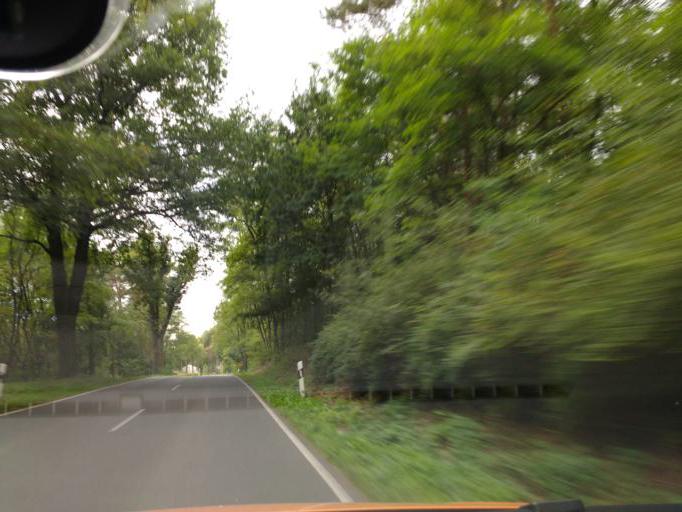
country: DE
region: Brandenburg
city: Reichenwalde
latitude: 52.2673
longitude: 14.0097
